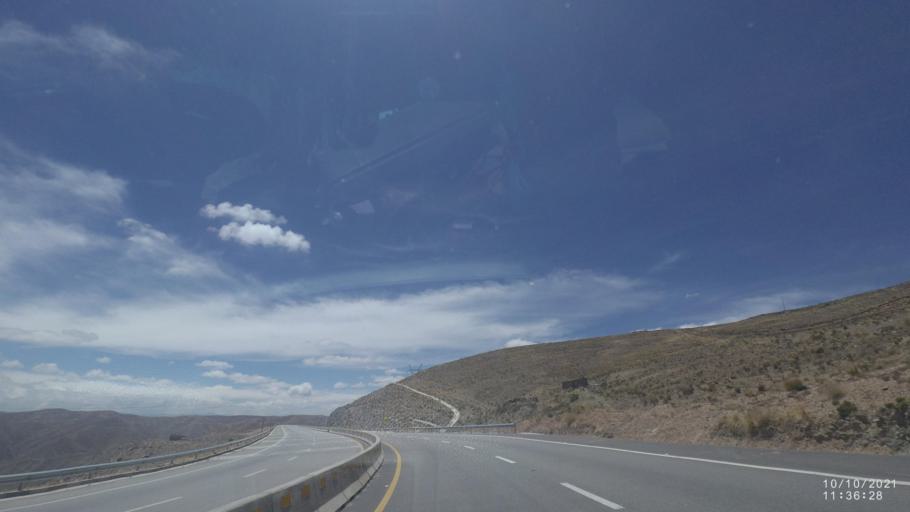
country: BO
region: Cochabamba
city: Colchani
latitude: -17.6706
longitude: -66.8158
